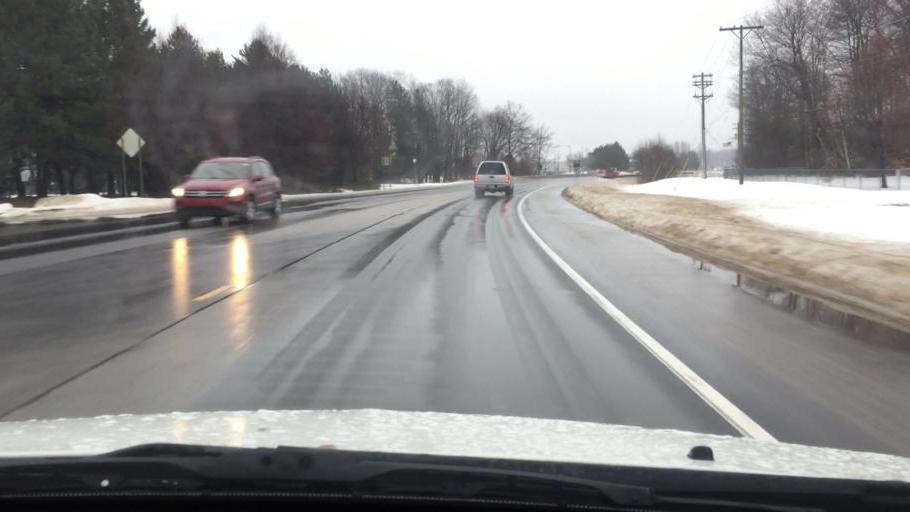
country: US
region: Michigan
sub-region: Charlevoix County
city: Charlevoix
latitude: 45.3019
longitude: -85.2583
